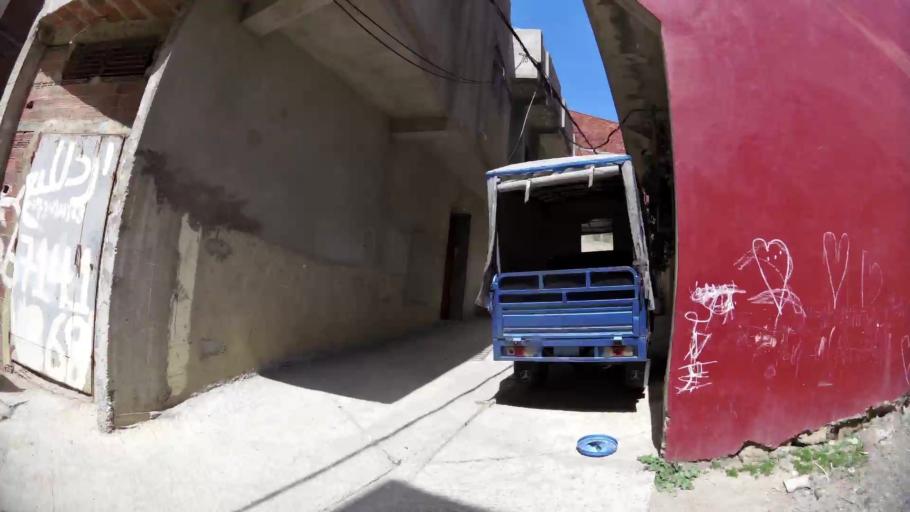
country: MA
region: Tanger-Tetouan
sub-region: Tanger-Assilah
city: Tangier
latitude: 35.7336
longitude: -5.8137
